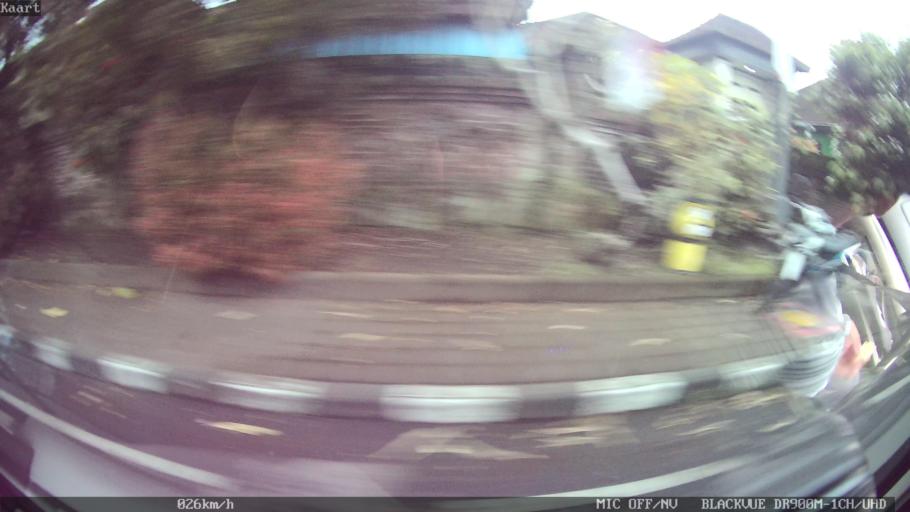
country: ID
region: Bali
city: Banjar Cemenggon
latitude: -8.5429
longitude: 115.1984
